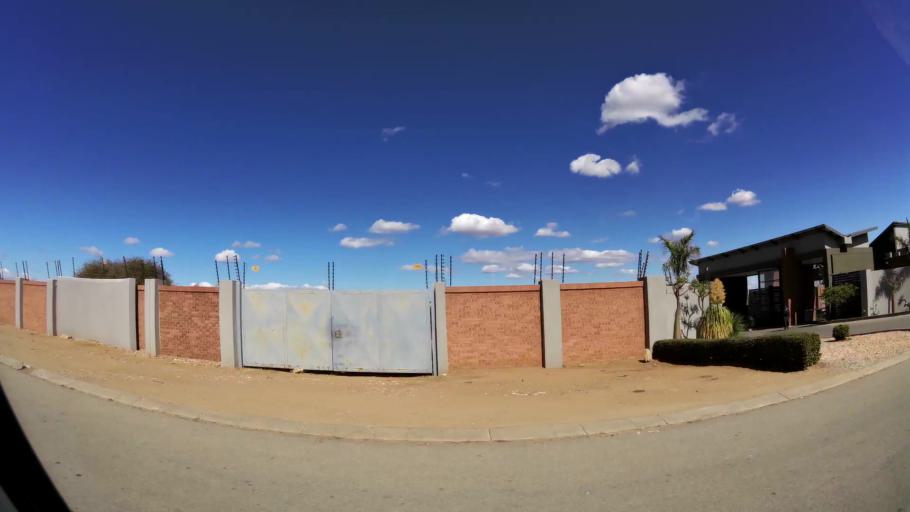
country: ZA
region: Limpopo
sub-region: Capricorn District Municipality
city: Polokwane
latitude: -23.9002
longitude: 29.4896
